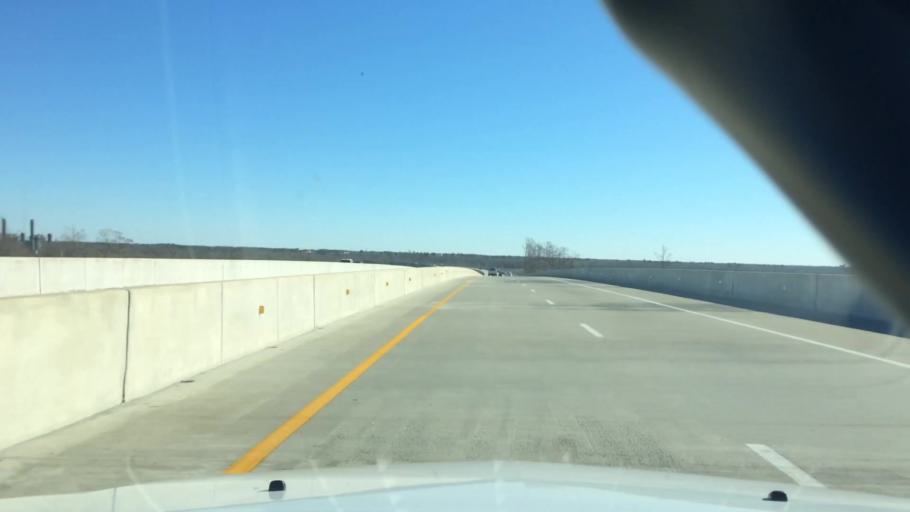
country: US
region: North Carolina
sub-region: Brunswick County
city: Navassa
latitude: 34.2731
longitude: -78.0023
